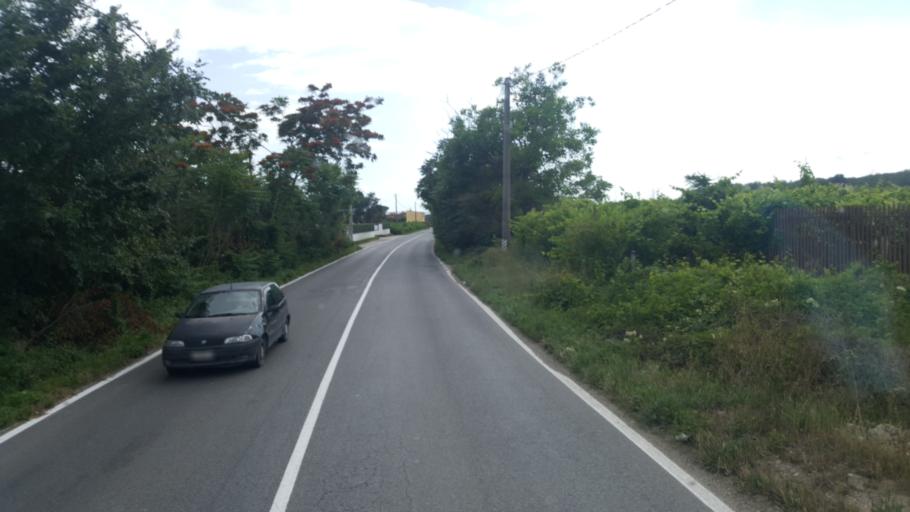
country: IT
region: Campania
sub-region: Provincia di Napoli
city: Acerra
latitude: 40.9715
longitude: 14.3888
